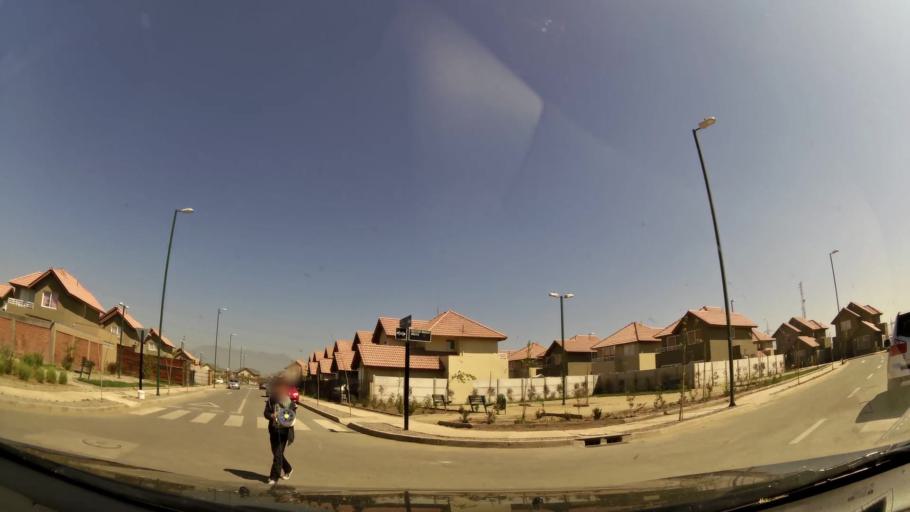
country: CL
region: Santiago Metropolitan
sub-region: Provincia de Chacabuco
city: Chicureo Abajo
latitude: -33.3219
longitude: -70.7550
